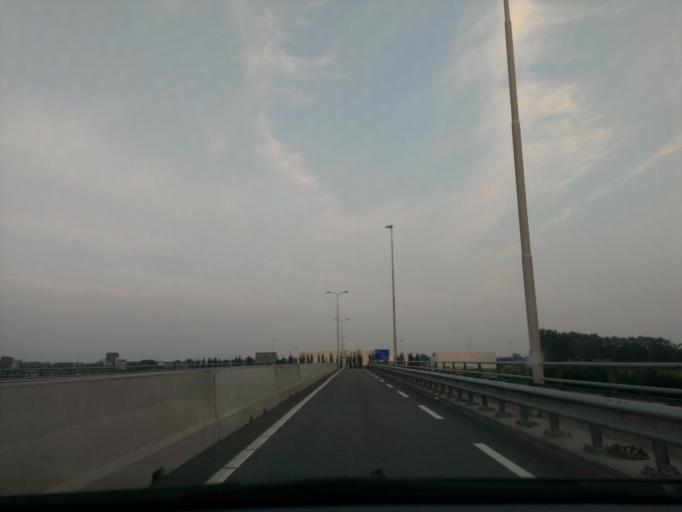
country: NL
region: Gelderland
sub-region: Gemeente Nijkerk
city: Nijkerk
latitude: 52.2107
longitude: 5.4432
